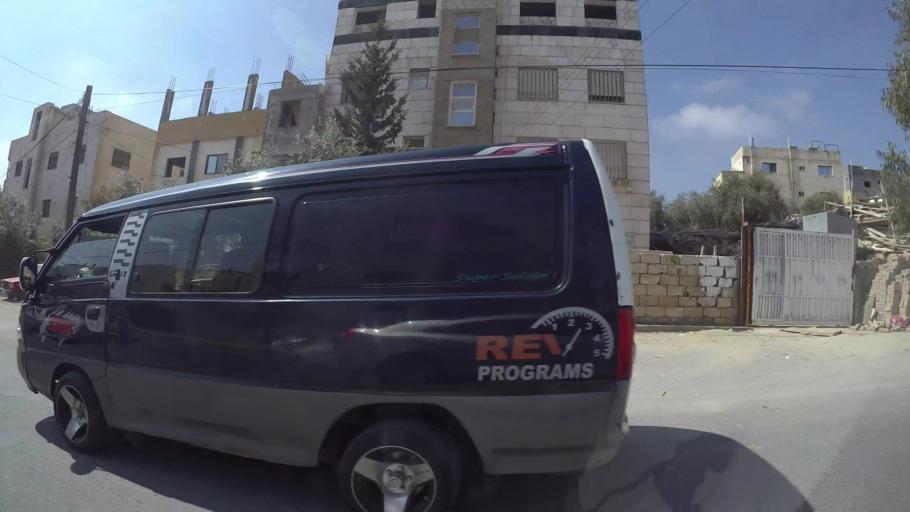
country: JO
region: Amman
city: Al Bunayyat ash Shamaliyah
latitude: 31.9015
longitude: 35.9059
